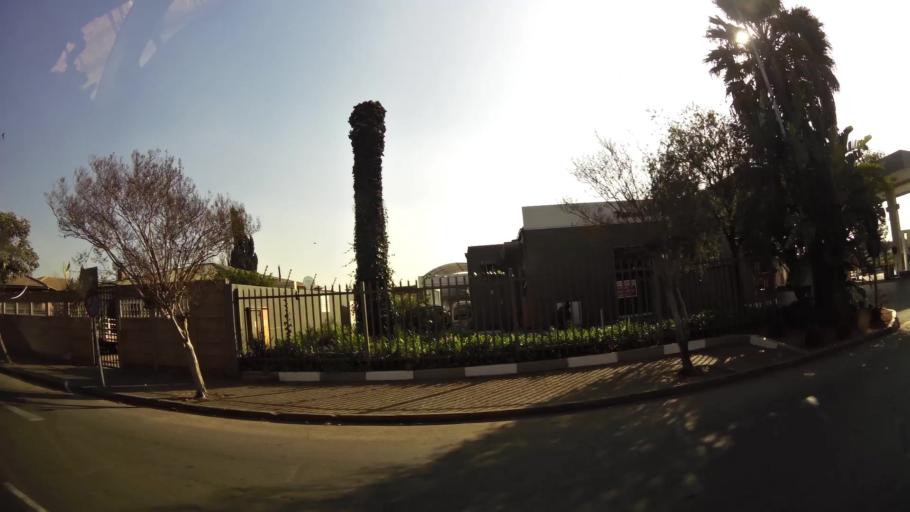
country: ZA
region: Gauteng
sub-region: West Rand District Municipality
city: Randfontein
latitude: -26.1749
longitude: 27.7077
